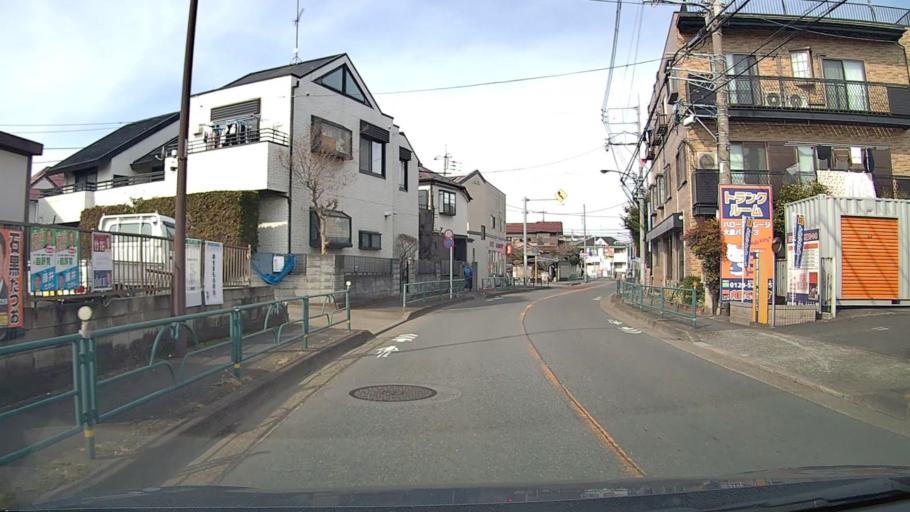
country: JP
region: Tokyo
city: Nishi-Tokyo-shi
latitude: 35.7577
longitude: 139.5780
